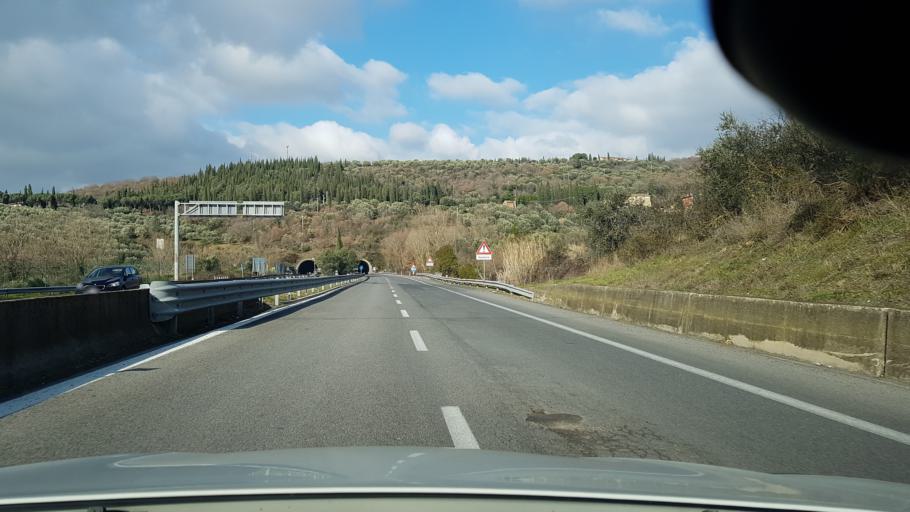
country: IT
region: Umbria
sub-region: Provincia di Perugia
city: Passignano sul Trasimeno
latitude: 43.1876
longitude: 12.1529
